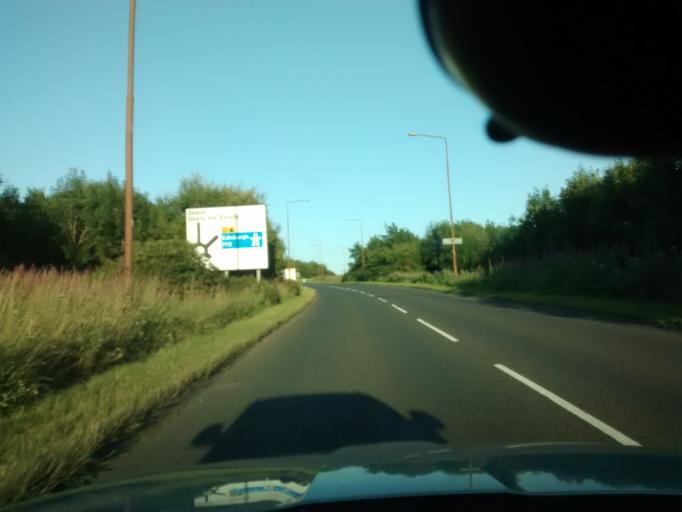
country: GB
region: Scotland
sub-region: West Lothian
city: Bathgate
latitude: 55.8973
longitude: -3.5988
